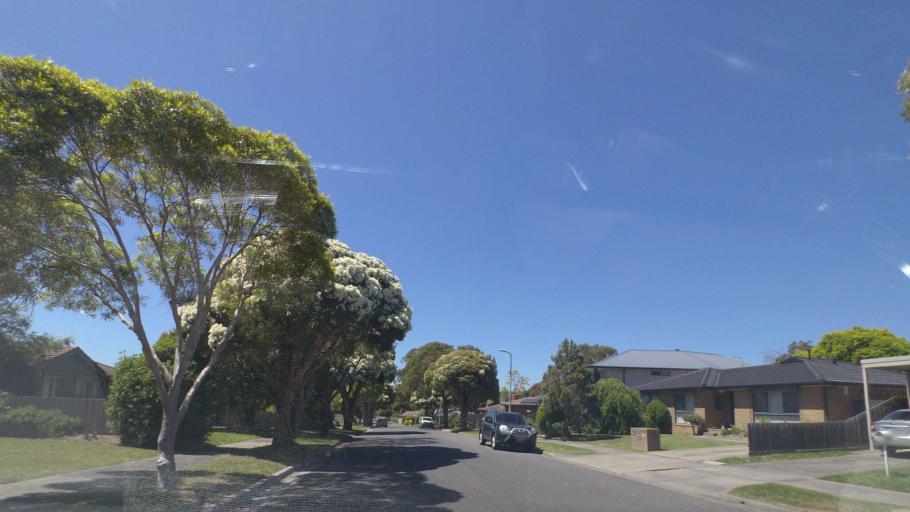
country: AU
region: Victoria
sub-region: Knox
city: Knoxfield
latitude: -37.8921
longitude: 145.2633
